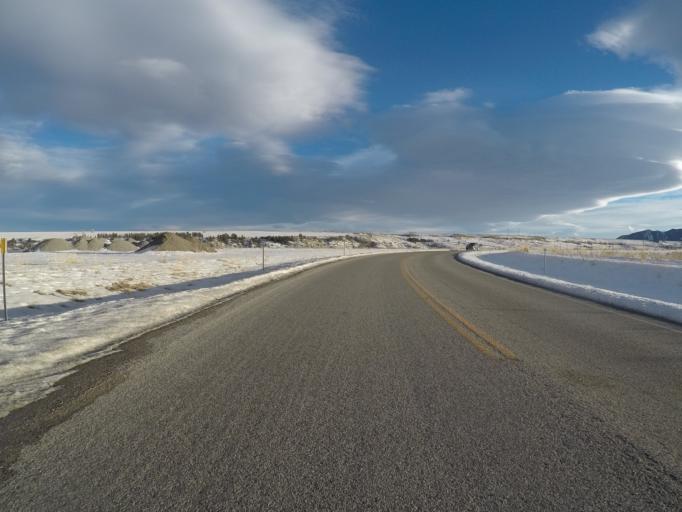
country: US
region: Montana
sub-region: Carbon County
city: Red Lodge
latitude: 45.1907
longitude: -109.2539
